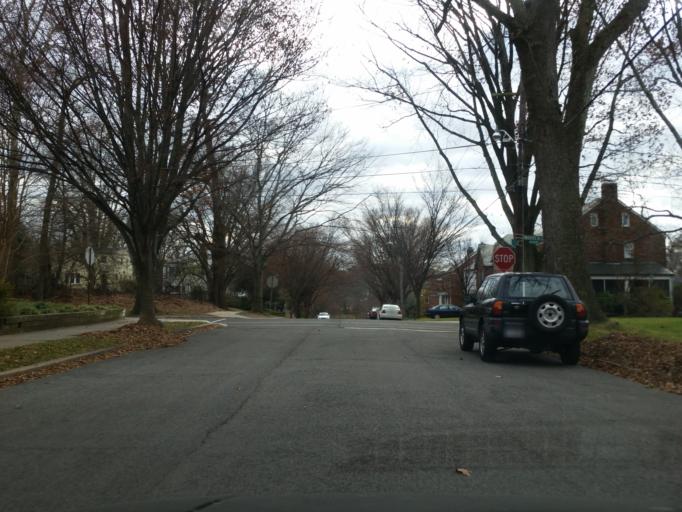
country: US
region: Maryland
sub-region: Montgomery County
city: Friendship Village
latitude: 38.9451
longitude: -77.0887
